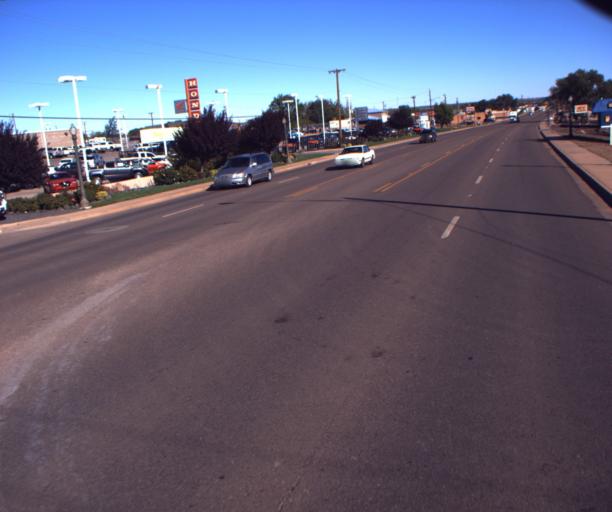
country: US
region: Arizona
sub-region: Navajo County
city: Snowflake
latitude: 34.4970
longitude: -110.0788
